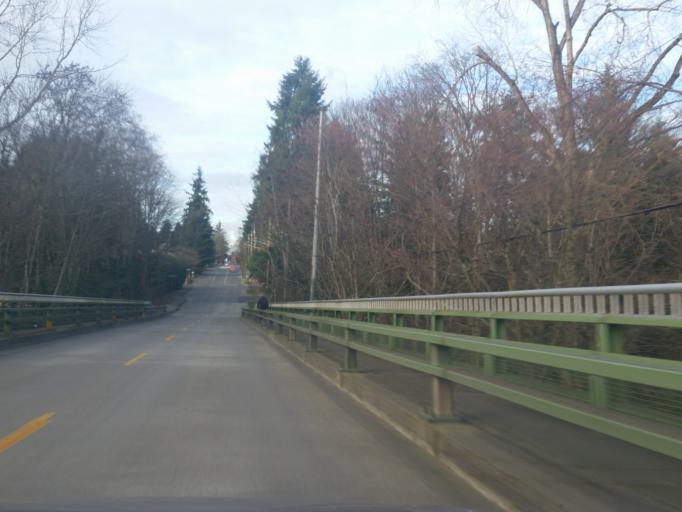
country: US
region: Washington
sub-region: King County
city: Shoreline
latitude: 47.7053
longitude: -122.3125
